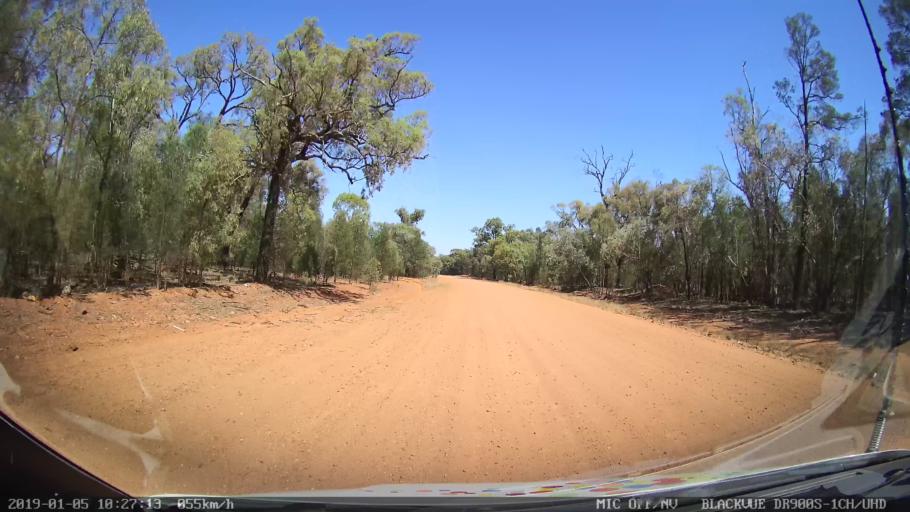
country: AU
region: New South Wales
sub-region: Gilgandra
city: Gilgandra
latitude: -31.5507
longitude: 148.9487
